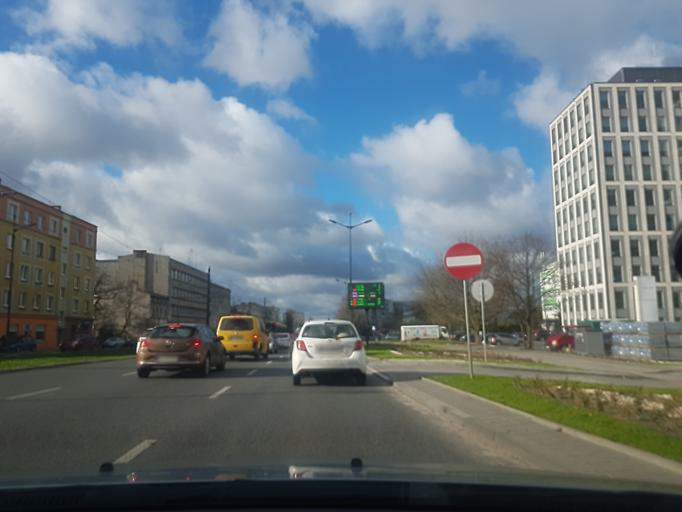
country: PL
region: Lodz Voivodeship
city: Lodz
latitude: 51.7622
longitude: 19.4918
